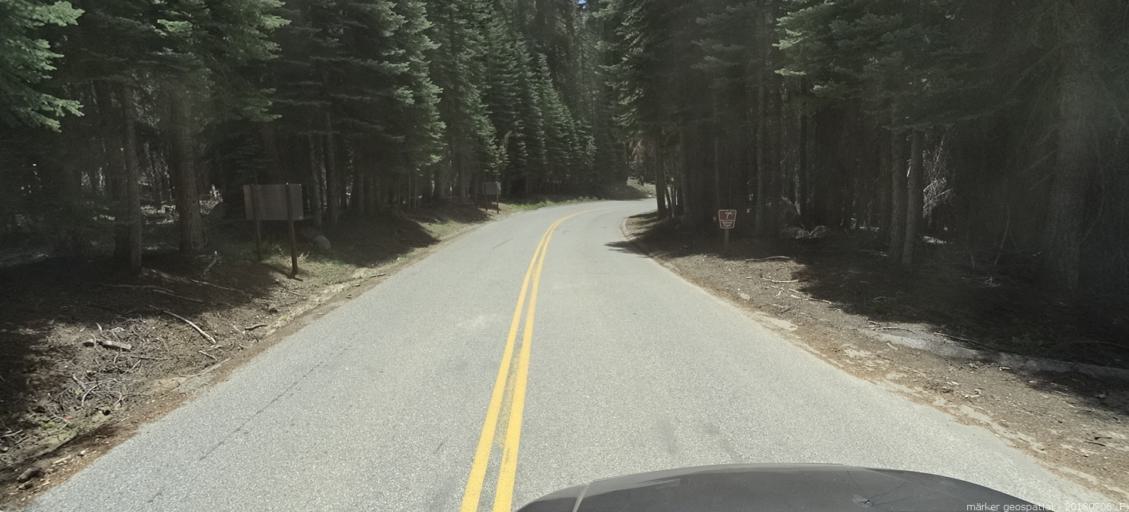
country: US
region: California
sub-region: Madera County
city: Oakhurst
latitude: 37.4150
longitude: -119.4950
